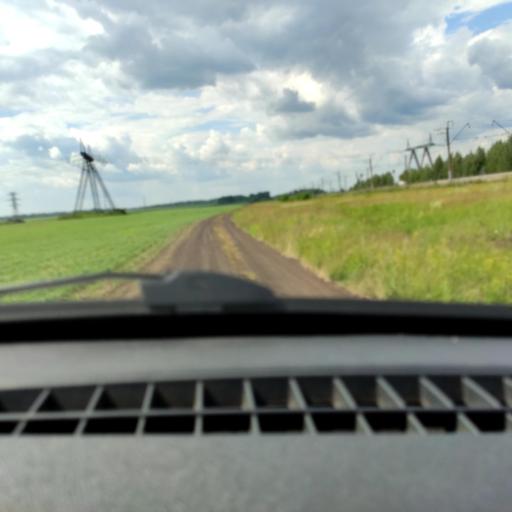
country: RU
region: Bashkortostan
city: Kabakovo
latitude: 54.5096
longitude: 56.1142
